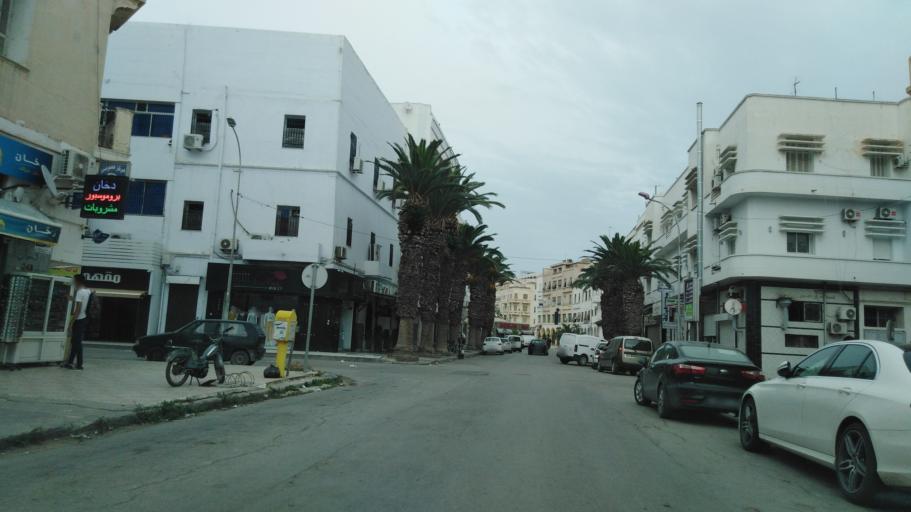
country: TN
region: Safaqis
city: Sfax
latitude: 34.7328
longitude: 10.7613
